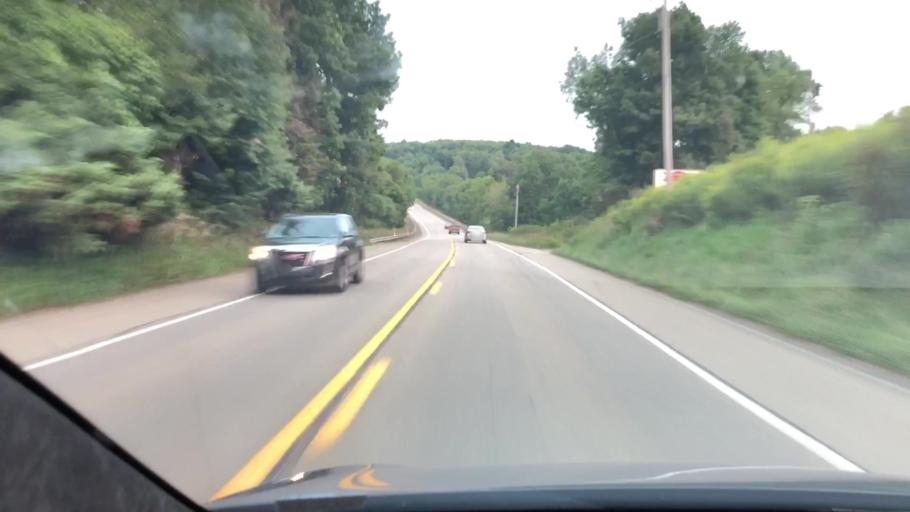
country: US
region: Pennsylvania
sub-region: Butler County
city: Shanor-Northvue
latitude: 40.9168
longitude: -79.9433
